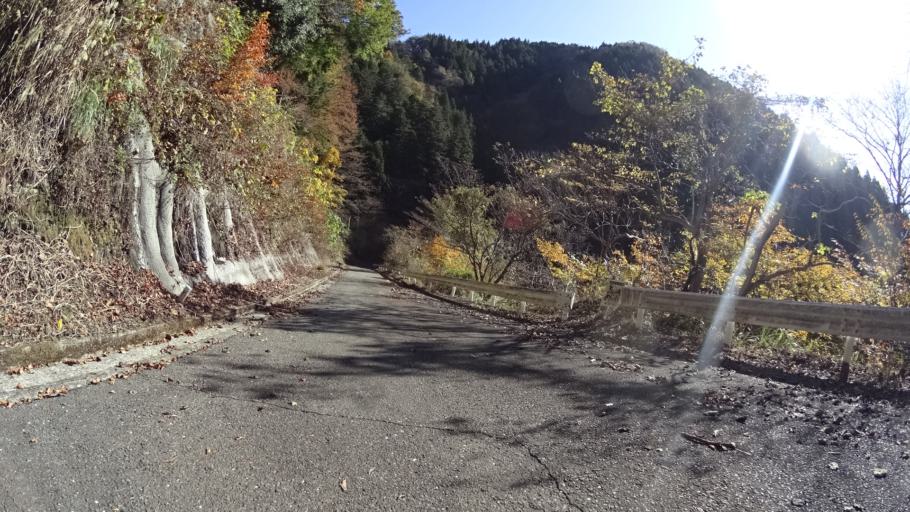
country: JP
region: Kanagawa
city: Atsugi
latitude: 35.5034
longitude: 139.2757
